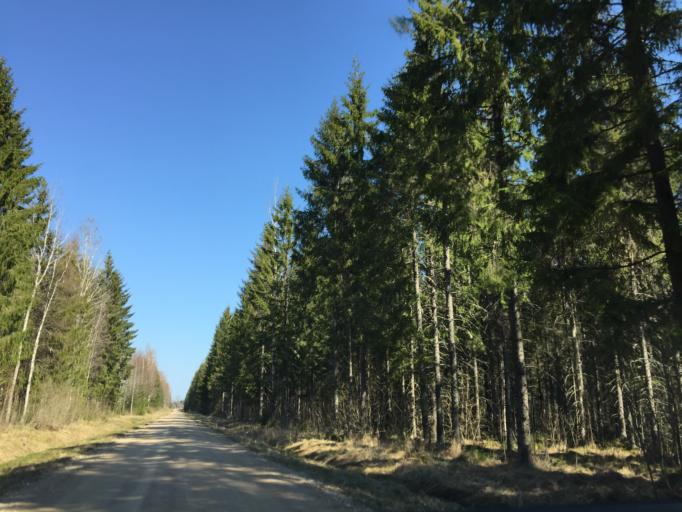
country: EE
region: Tartu
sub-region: Alatskivi vald
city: Kallaste
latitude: 58.5591
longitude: 26.9401
